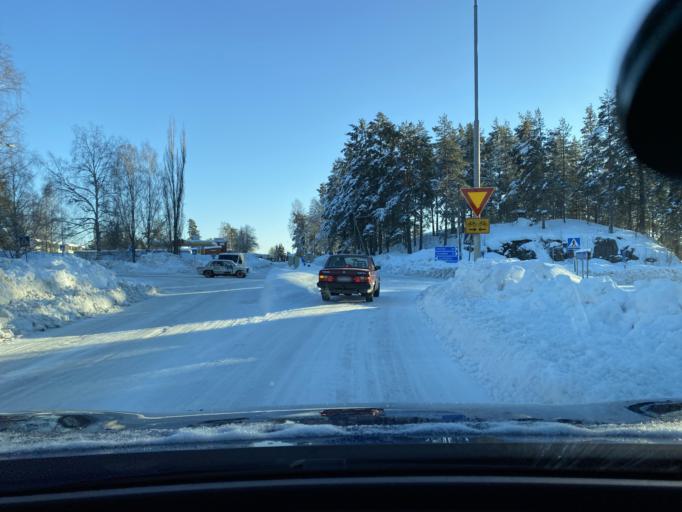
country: FI
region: Southern Savonia
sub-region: Mikkeli
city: Kangasniemi
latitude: 61.9912
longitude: 26.6343
